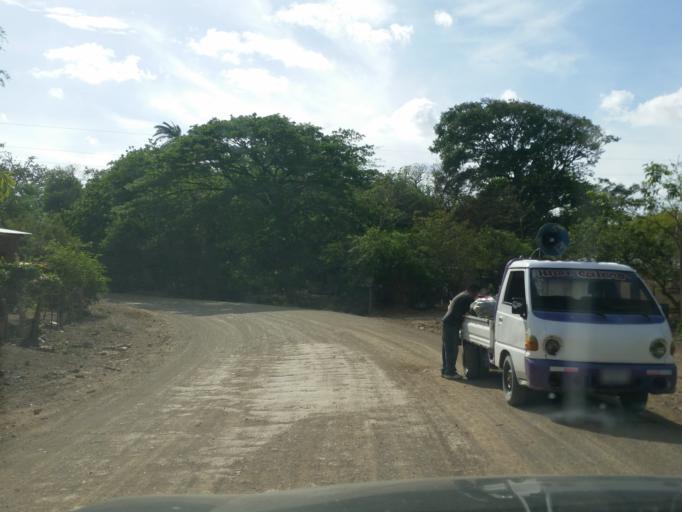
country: NI
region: Rivas
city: Tola
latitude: 11.4537
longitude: -86.0674
